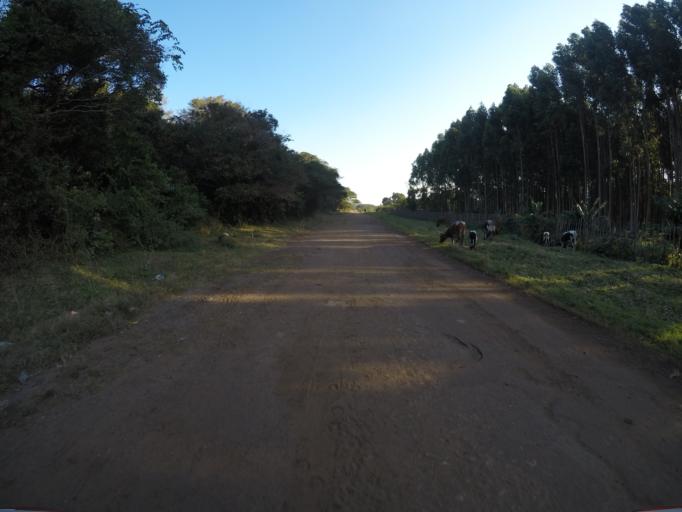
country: ZA
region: KwaZulu-Natal
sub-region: uThungulu District Municipality
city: KwaMbonambi
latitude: -28.6974
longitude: 32.1951
